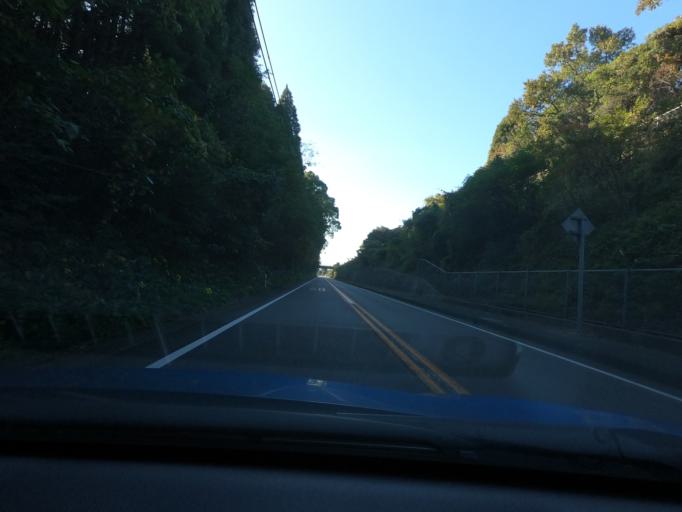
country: JP
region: Kumamoto
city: Minamata
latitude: 32.1621
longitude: 130.3727
